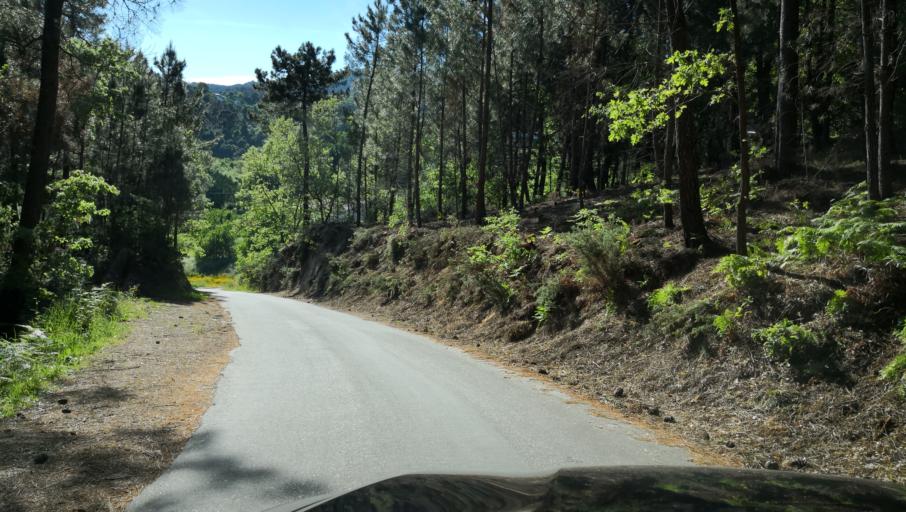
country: PT
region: Vila Real
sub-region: Vila Real
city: Vila Real
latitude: 41.3376
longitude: -7.7368
